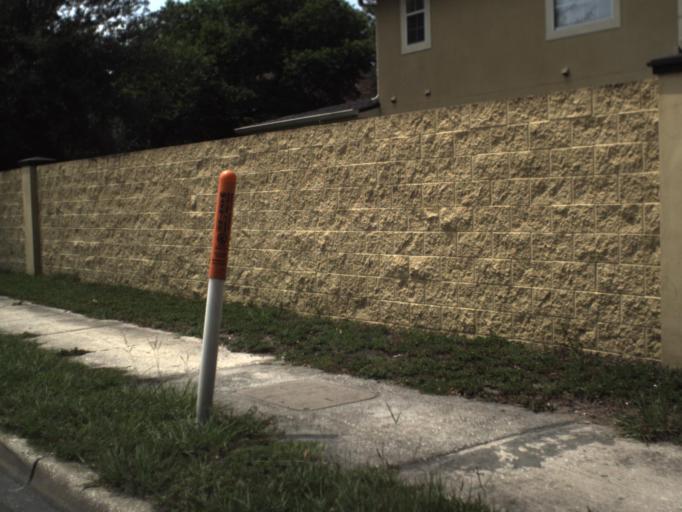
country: US
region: Florida
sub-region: Hillsborough County
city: Tampa
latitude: 27.9211
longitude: -82.5060
